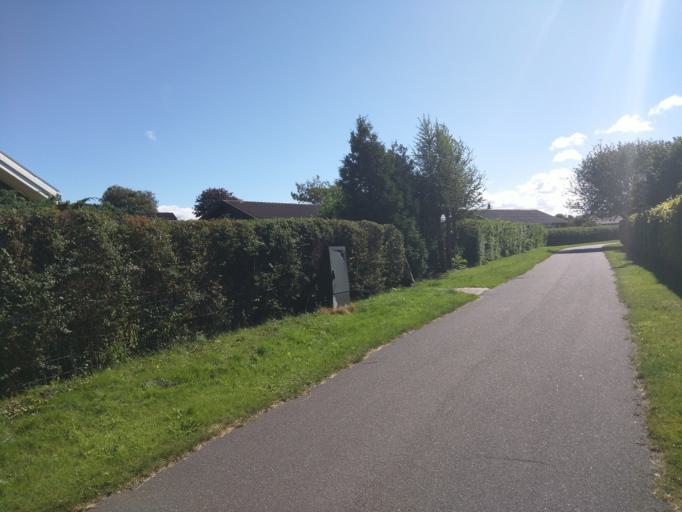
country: DK
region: Central Jutland
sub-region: Viborg Kommune
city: Viborg
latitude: 56.4692
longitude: 9.3844
